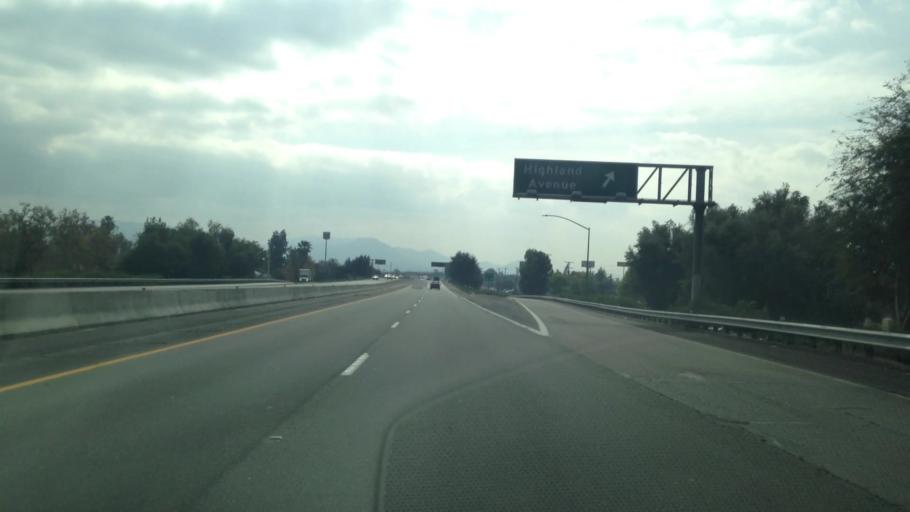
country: US
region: California
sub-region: San Bernardino County
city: San Bernardino
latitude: 34.1399
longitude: -117.3027
